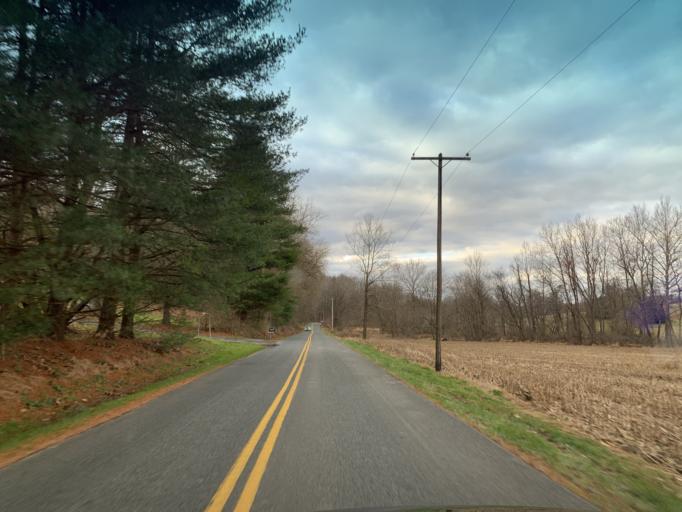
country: US
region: Maryland
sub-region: Harford County
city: Jarrettsville
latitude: 39.6589
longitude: -76.4426
